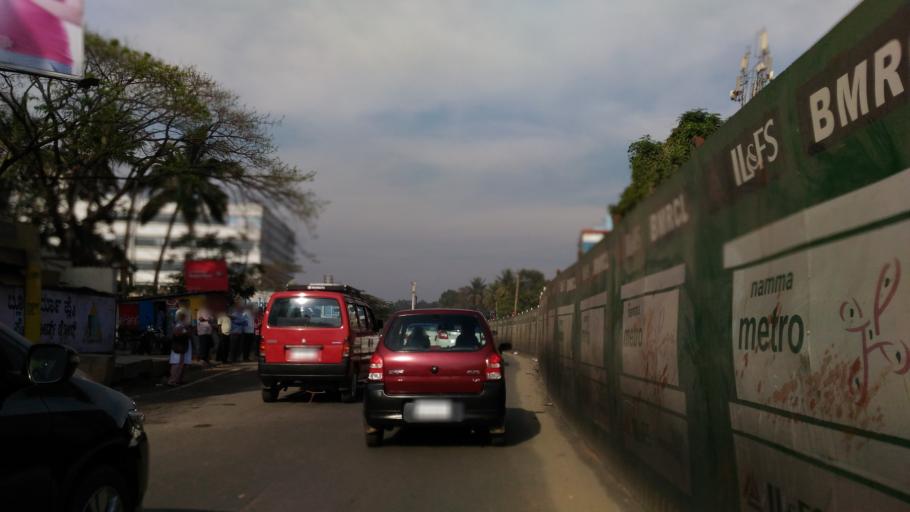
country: IN
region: Karnataka
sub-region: Bangalore Urban
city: Bangalore
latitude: 12.9363
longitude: 77.5175
